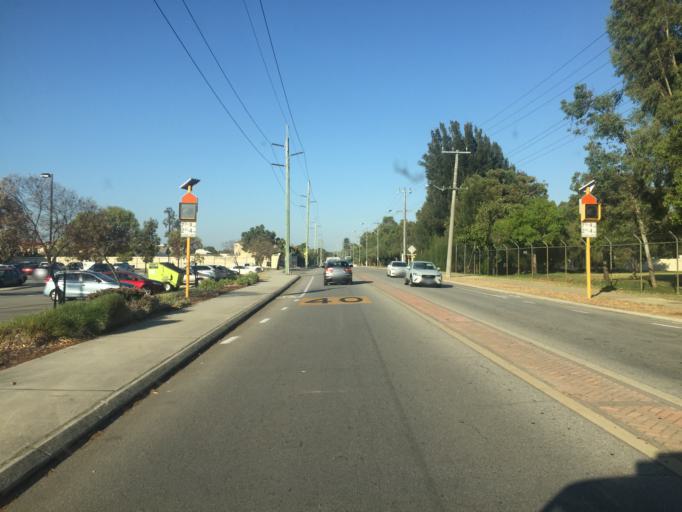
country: AU
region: Western Australia
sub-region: Belmont
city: Belmont
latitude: -31.9581
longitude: 115.9318
